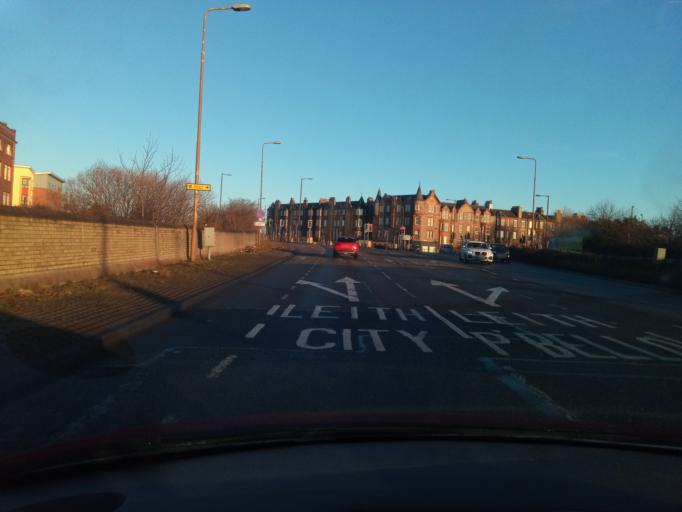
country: GB
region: Scotland
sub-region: West Lothian
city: Seafield
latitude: 55.9566
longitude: -3.1232
